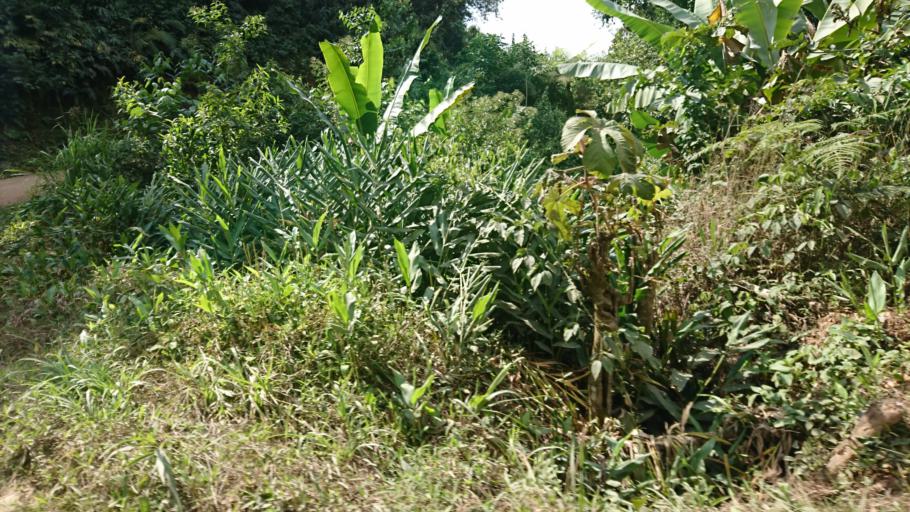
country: BO
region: La Paz
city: Coroico
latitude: -16.1245
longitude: -67.7631
